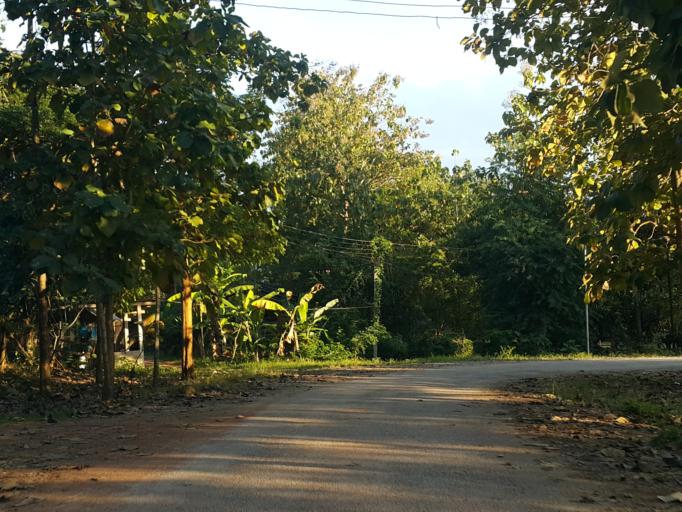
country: TH
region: Lampang
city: Lampang
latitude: 18.4202
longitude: 99.5539
